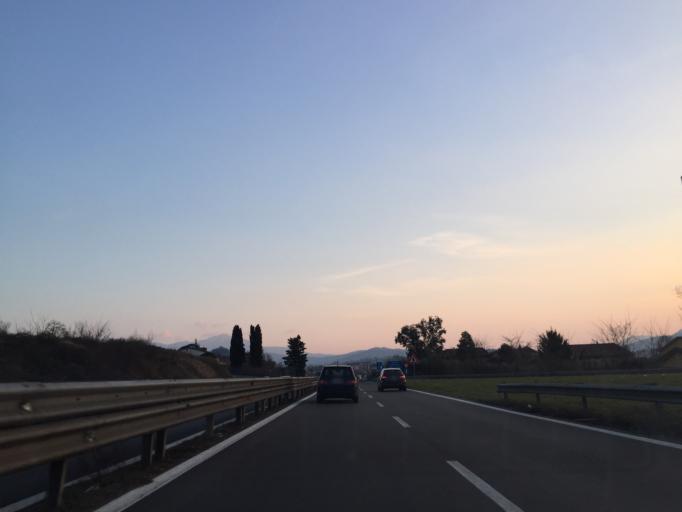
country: IT
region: Campania
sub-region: Provincia di Avellino
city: Manocalzati
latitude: 40.9360
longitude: 14.8316
